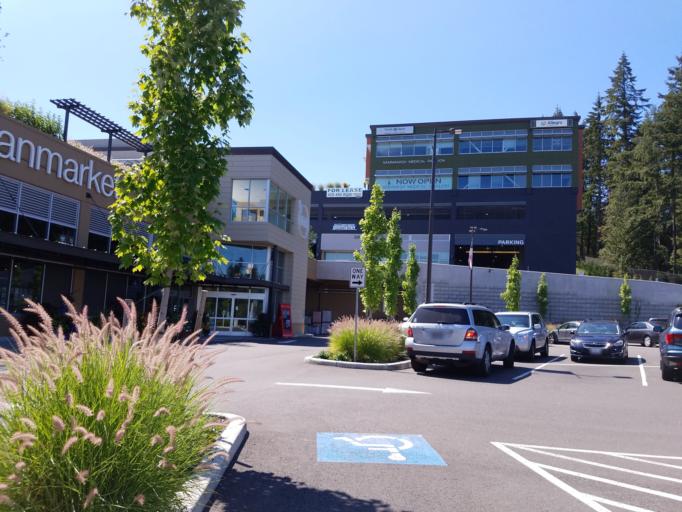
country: US
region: Washington
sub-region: King County
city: City of Sammamish
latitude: 47.6061
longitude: -122.0360
